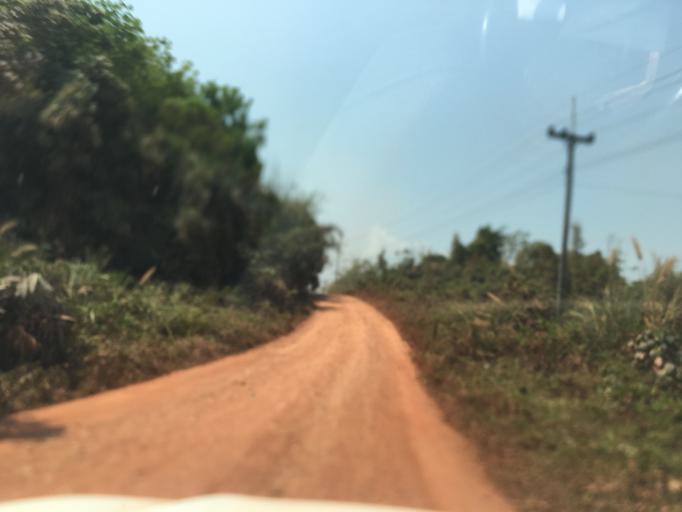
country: LA
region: Bolikhamxai
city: Bolikhan
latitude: 18.7505
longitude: 103.6070
